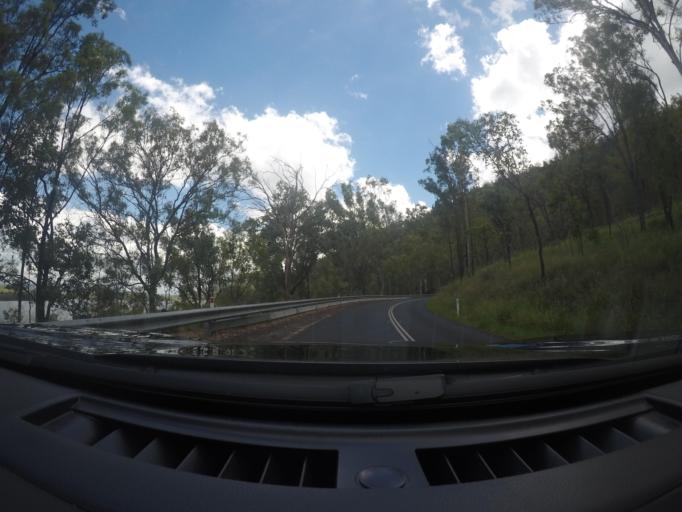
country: AU
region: Queensland
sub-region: Moreton Bay
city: Woodford
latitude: -27.0911
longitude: 152.5628
